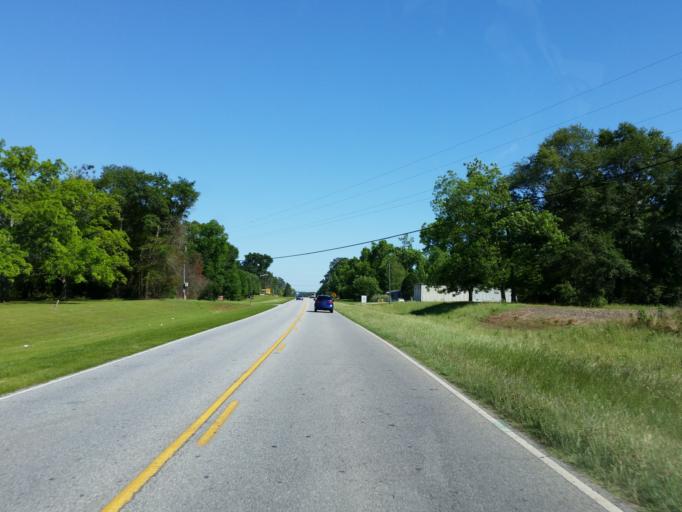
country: US
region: Georgia
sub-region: Lowndes County
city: Remerton
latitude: 30.9066
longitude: -83.3422
